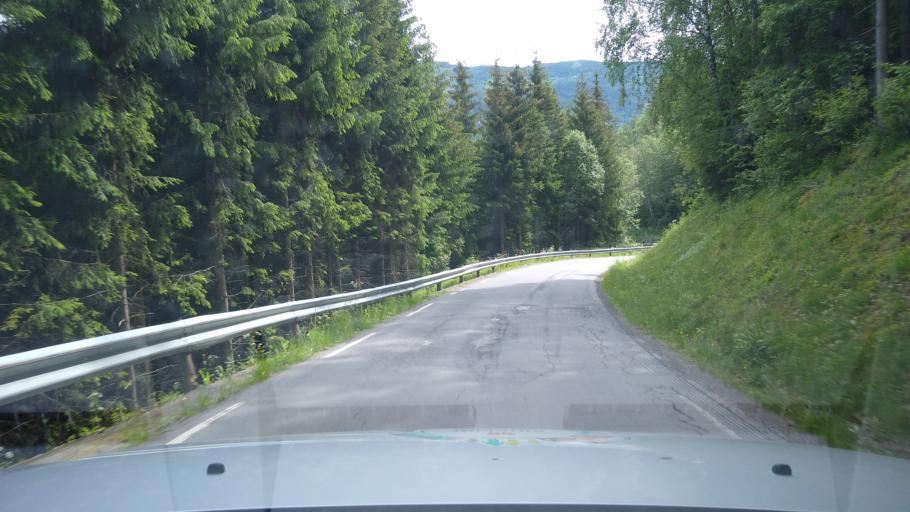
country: NO
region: Oppland
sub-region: Ringebu
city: Ringebu
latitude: 61.5194
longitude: 10.1366
